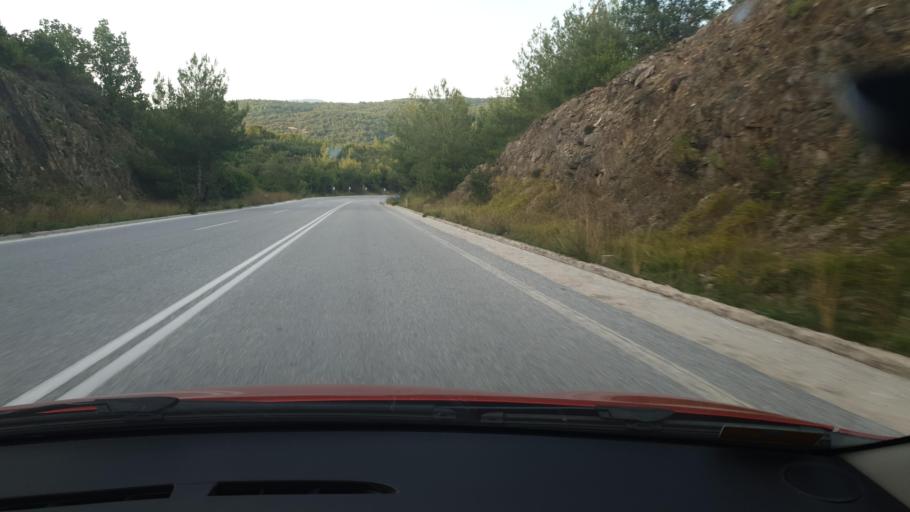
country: GR
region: Central Macedonia
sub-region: Nomos Chalkidikis
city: Polygyros
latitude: 40.4210
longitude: 23.4209
